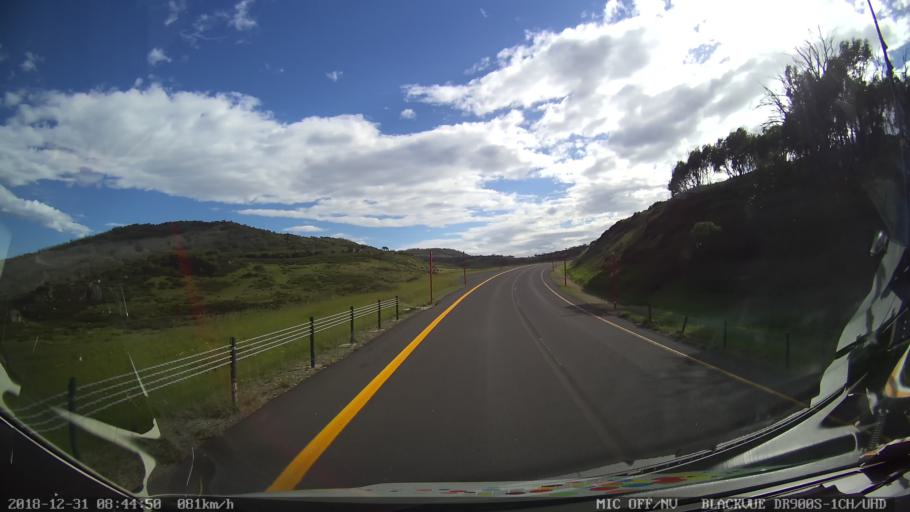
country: AU
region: New South Wales
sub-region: Snowy River
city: Jindabyne
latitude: -36.3803
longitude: 148.4584
